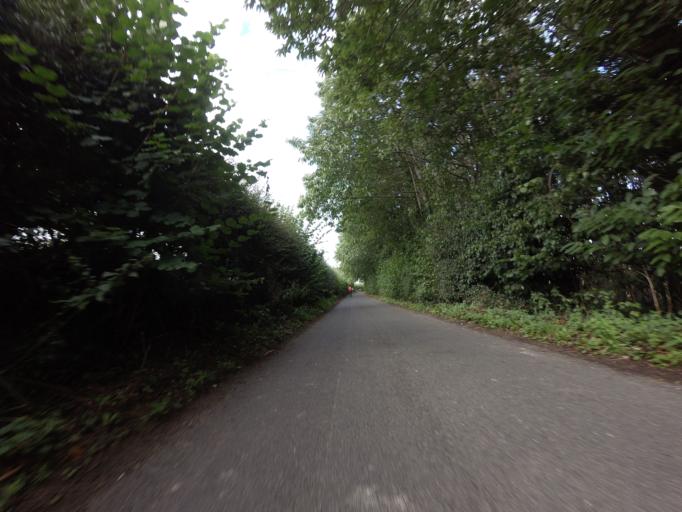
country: GB
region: England
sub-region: Kent
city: Shoreham
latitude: 51.3484
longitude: 0.1837
